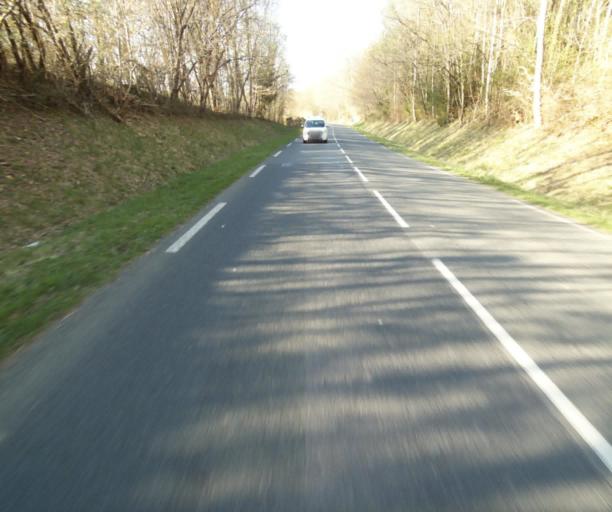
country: FR
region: Limousin
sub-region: Departement de la Correze
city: Seilhac
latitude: 45.3946
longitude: 1.7175
